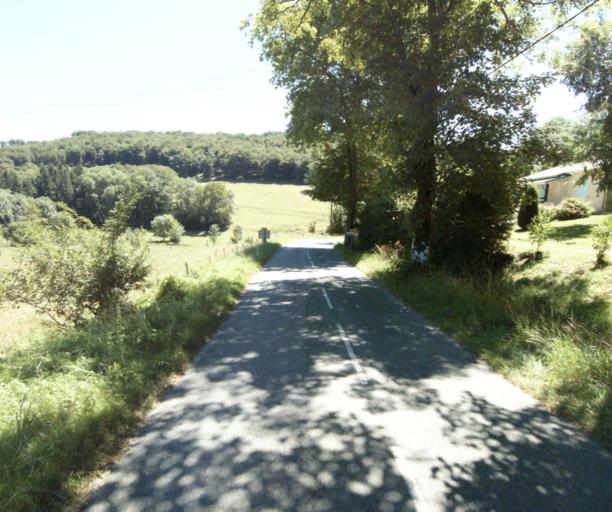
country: FR
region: Midi-Pyrenees
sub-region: Departement du Tarn
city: Dourgne
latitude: 43.4273
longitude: 2.1704
